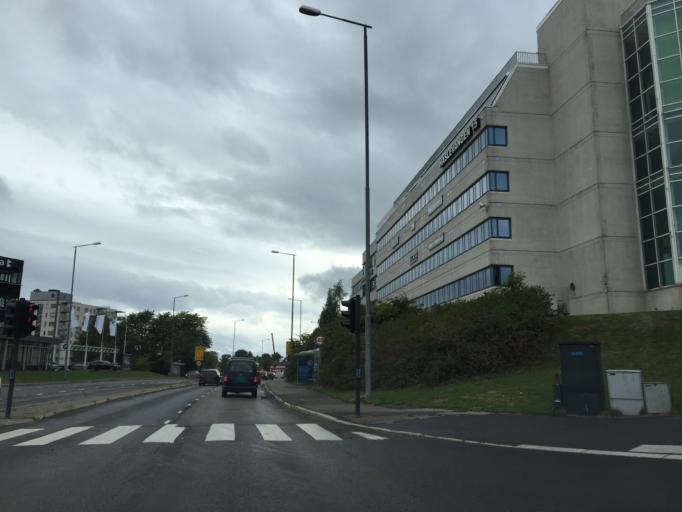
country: NO
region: Oslo
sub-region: Oslo
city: Oslo
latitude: 59.9256
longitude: 10.7949
